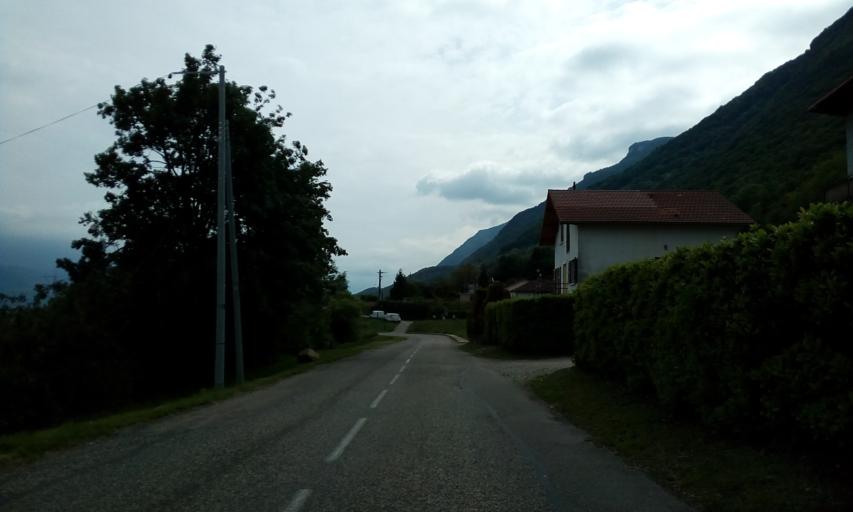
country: FR
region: Rhone-Alpes
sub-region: Departement de l'Isere
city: Saint-Vincent-de-Mercuze
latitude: 45.3853
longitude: 5.9527
